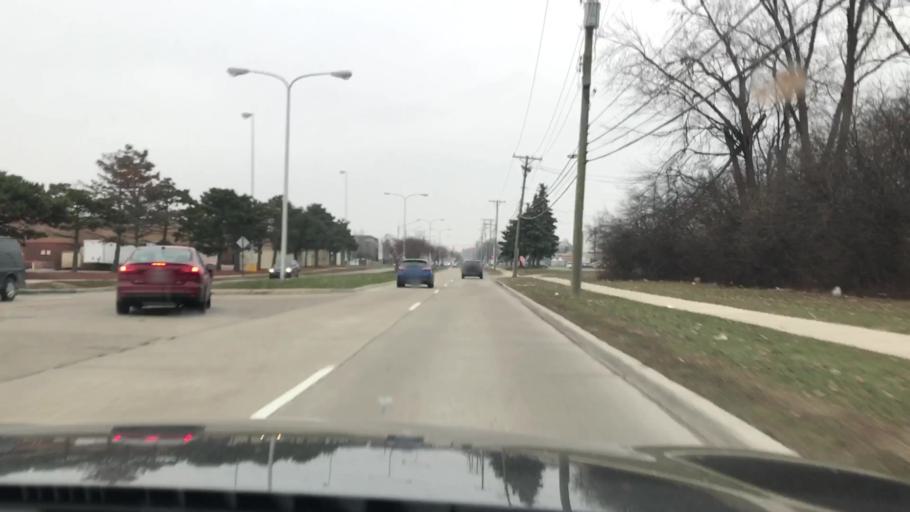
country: US
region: Michigan
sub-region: Oakland County
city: Clawson
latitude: 42.5273
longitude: -83.1101
